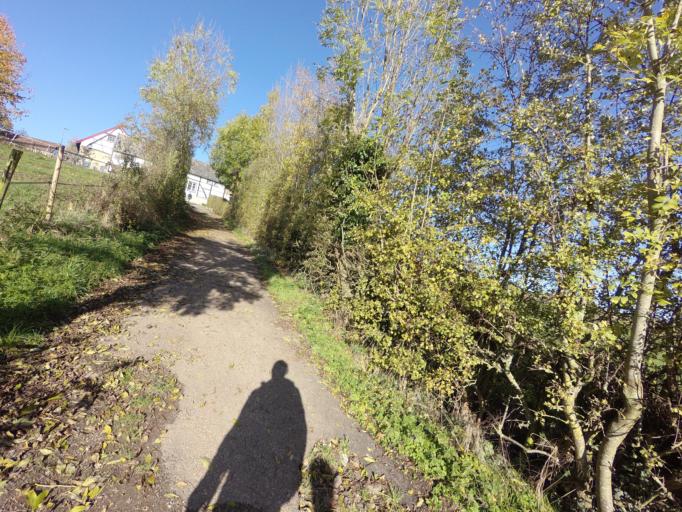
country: NL
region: Limburg
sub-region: Gemeente Voerendaal
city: Ubachsberg
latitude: 50.8368
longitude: 5.9330
